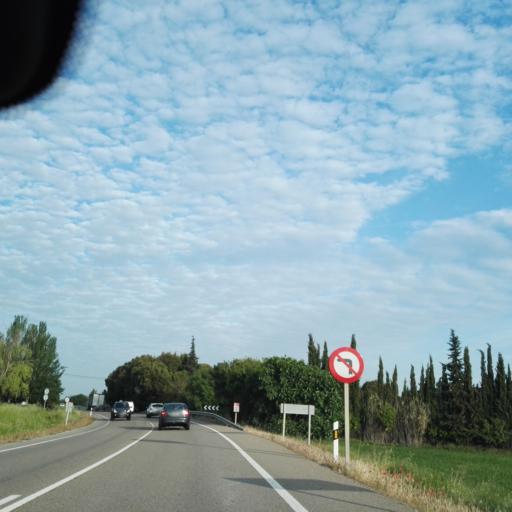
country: ES
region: Aragon
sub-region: Provincia de Zaragoza
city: Oliver-Valdefierro, Oliver, Valdefierro
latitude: 41.6637
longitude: -0.9667
